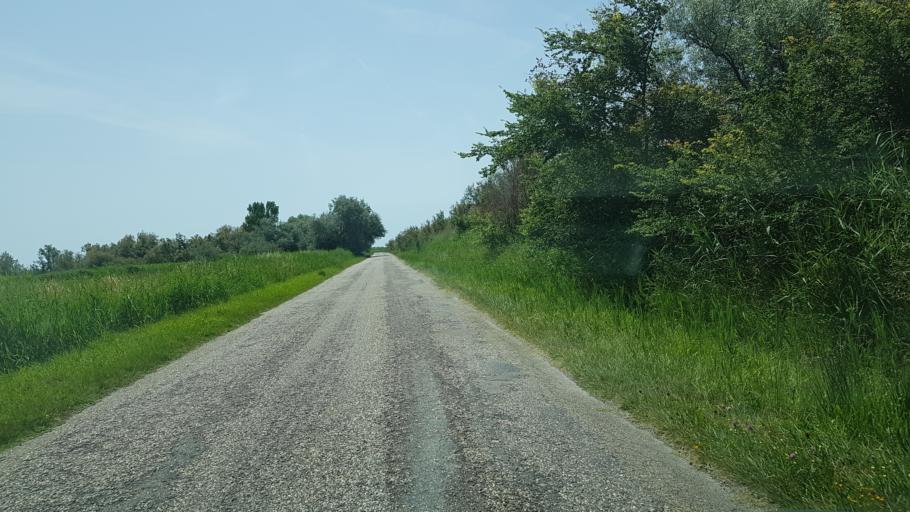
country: FR
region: Provence-Alpes-Cote d'Azur
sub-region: Departement des Bouches-du-Rhone
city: Arles
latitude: 43.5573
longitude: 4.6248
